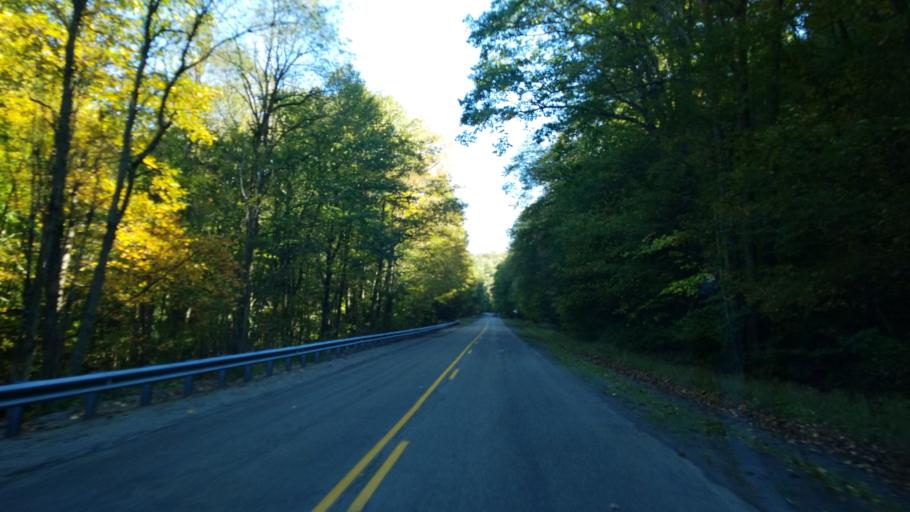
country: US
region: Pennsylvania
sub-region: Clearfield County
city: Shiloh
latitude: 41.2545
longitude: -78.3845
